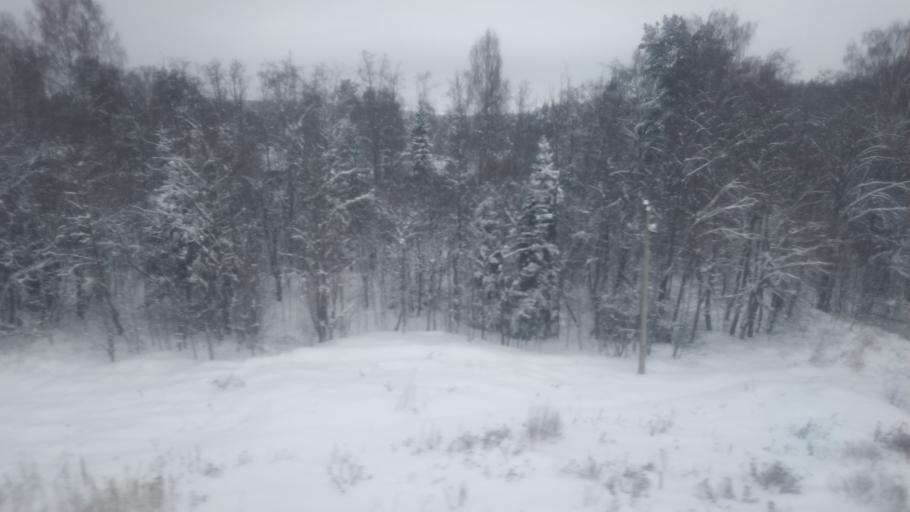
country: RU
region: Udmurtiya
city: Pychas
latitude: 56.5048
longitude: 52.4557
